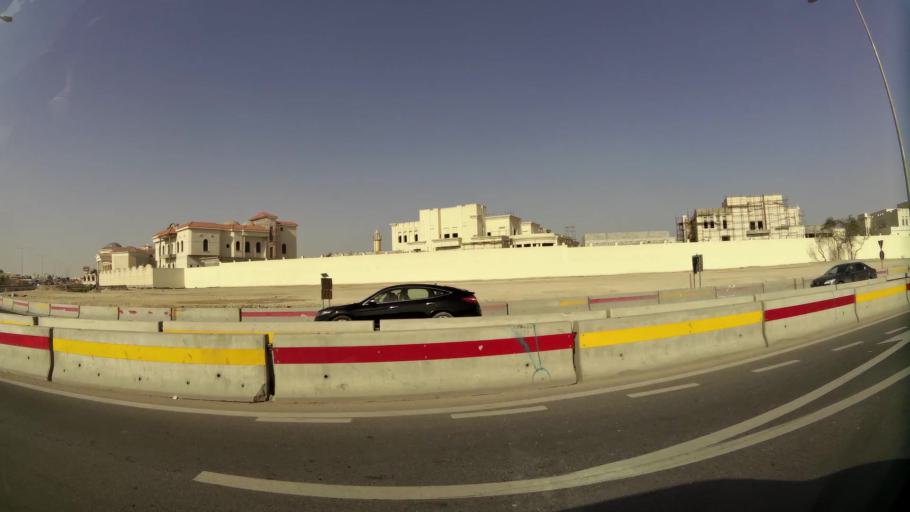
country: QA
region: Baladiyat ar Rayyan
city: Ar Rayyan
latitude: 25.3306
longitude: 51.4480
